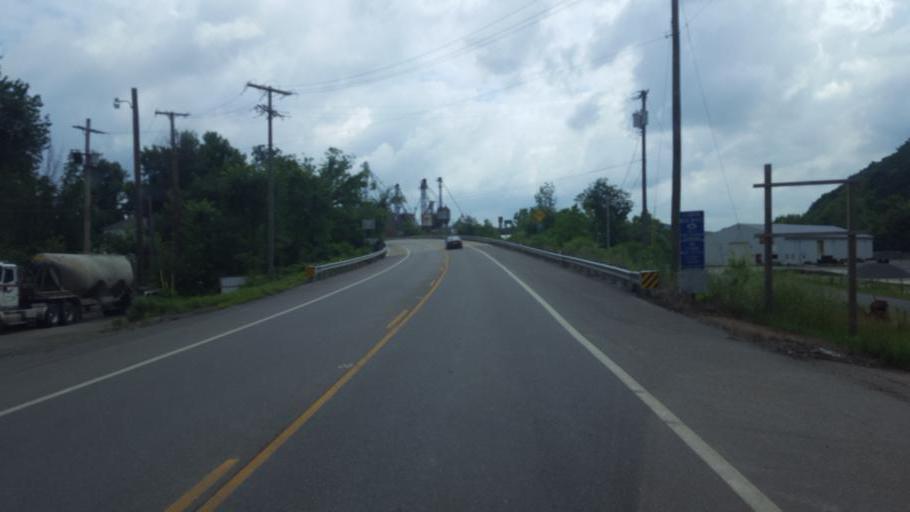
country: US
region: Ohio
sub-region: Columbiana County
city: Lisbon
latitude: 40.7670
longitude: -80.7751
